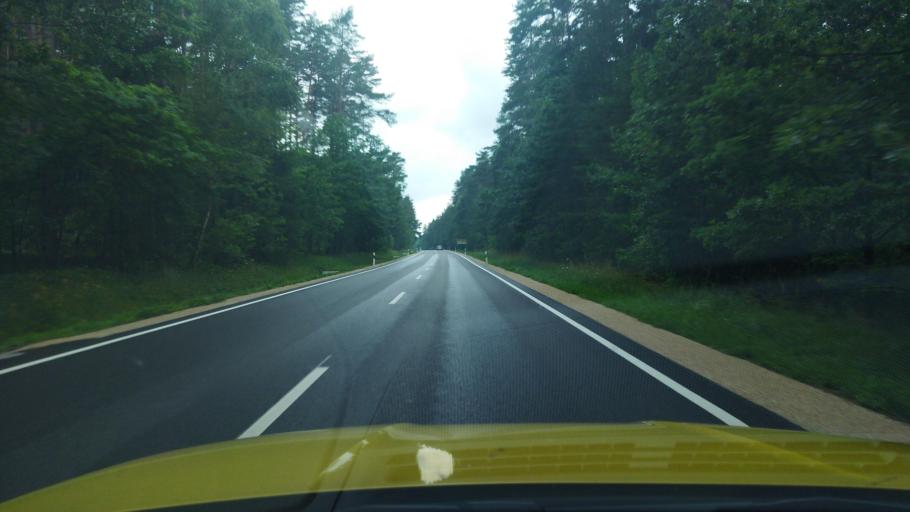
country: DE
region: Bavaria
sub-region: Regierungsbezirk Mittelfranken
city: Pfofeld
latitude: 49.1209
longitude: 10.8305
